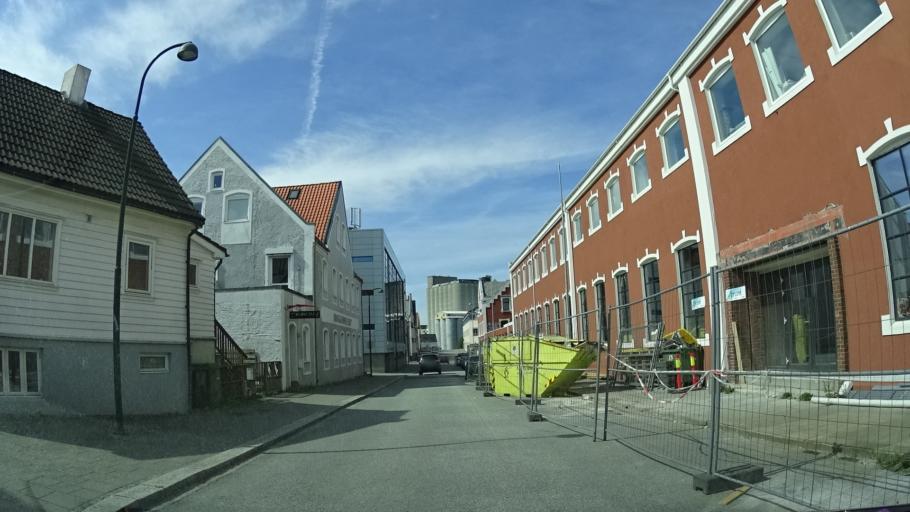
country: NO
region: Rogaland
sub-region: Stavanger
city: Stavanger
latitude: 58.9684
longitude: 5.7581
